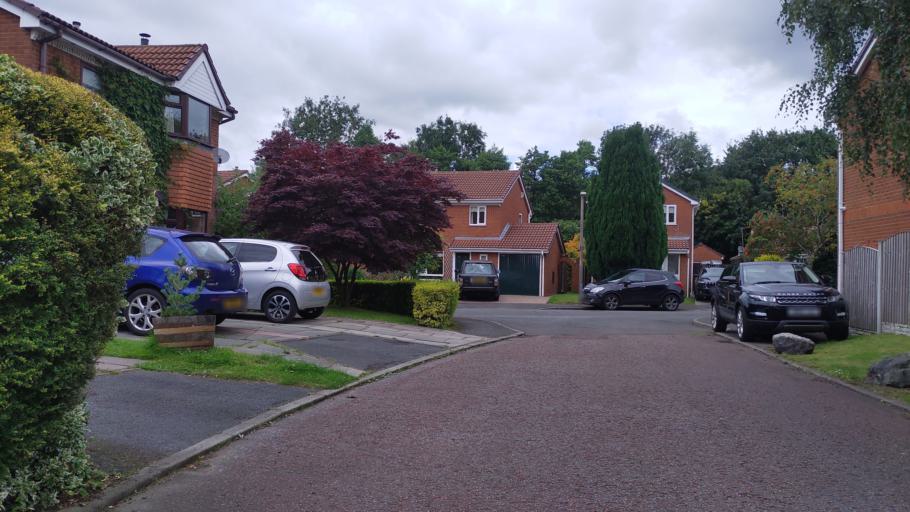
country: GB
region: England
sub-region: Lancashire
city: Coppull
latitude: 53.6350
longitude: -2.6391
